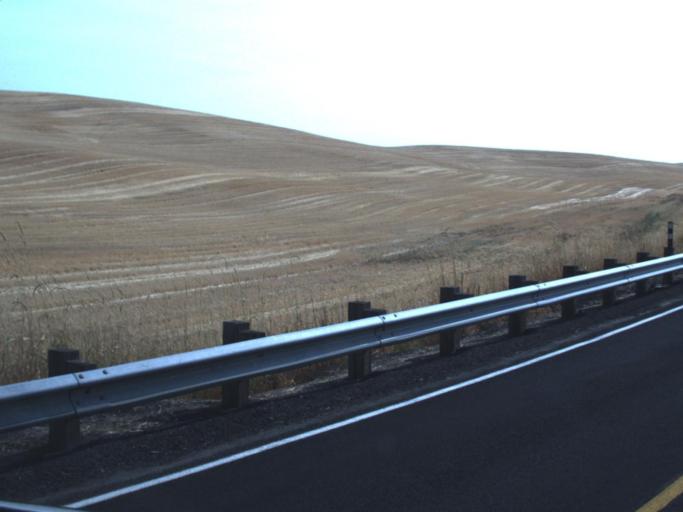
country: US
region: Washington
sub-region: Whitman County
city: Pullman
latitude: 46.9809
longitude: -117.1246
